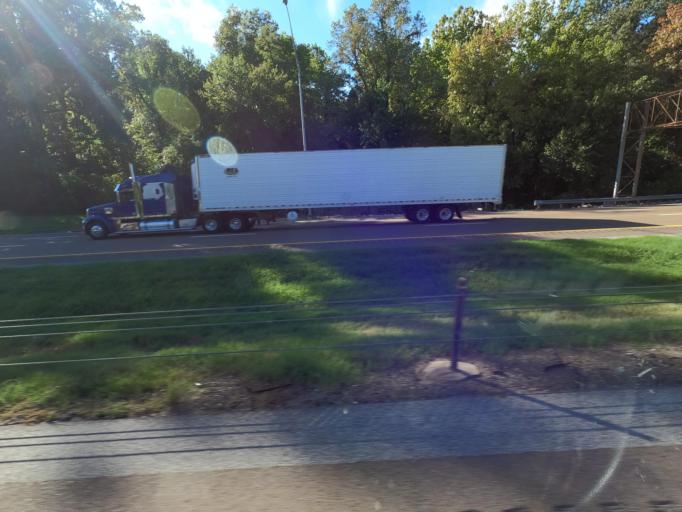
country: US
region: Tennessee
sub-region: Shelby County
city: New South Memphis
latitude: 35.0965
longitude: -90.0764
